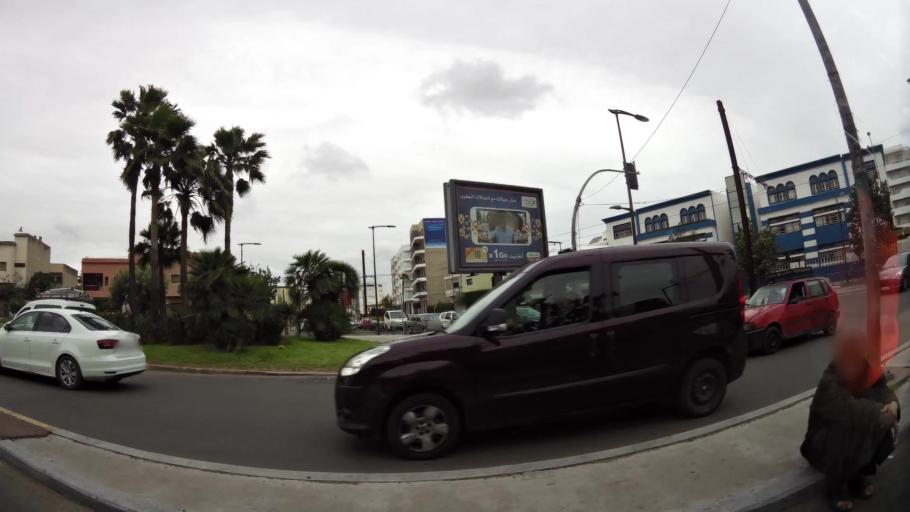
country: MA
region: Grand Casablanca
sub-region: Casablanca
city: Casablanca
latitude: 33.5688
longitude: -7.6152
